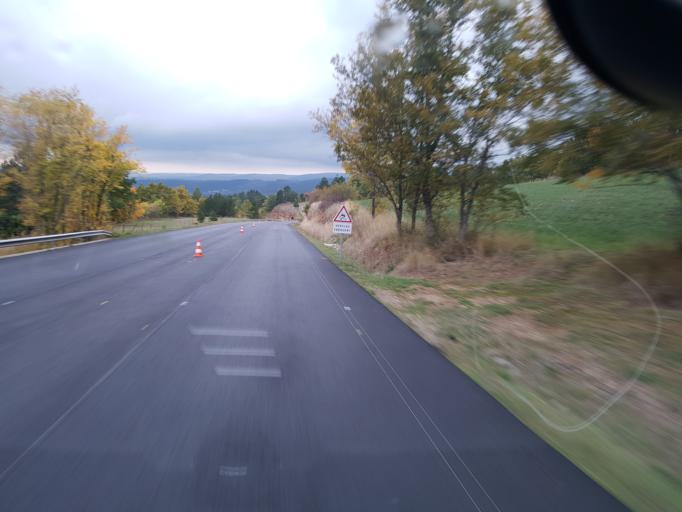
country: FR
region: Languedoc-Roussillon
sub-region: Departement de la Lozere
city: Mende
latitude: 44.5360
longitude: 3.5961
